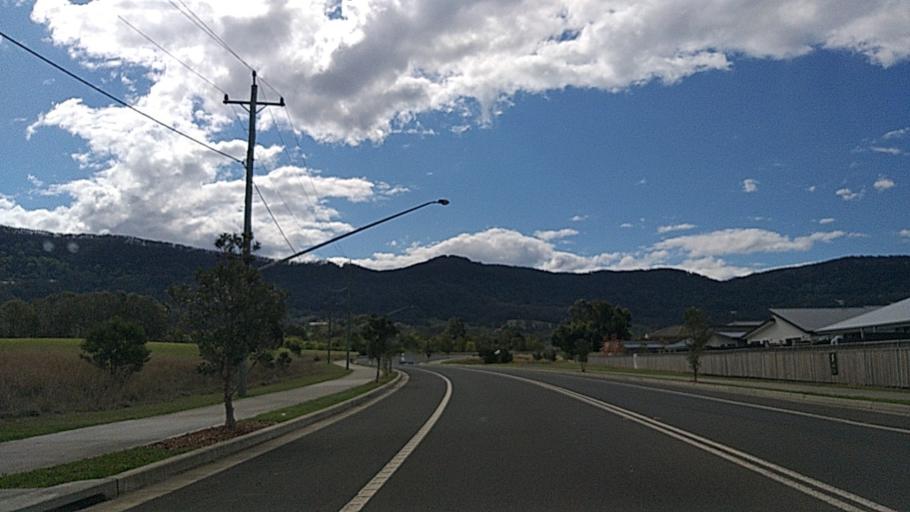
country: AU
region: New South Wales
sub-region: Wollongong
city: Dapto
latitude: -34.4820
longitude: 150.7668
